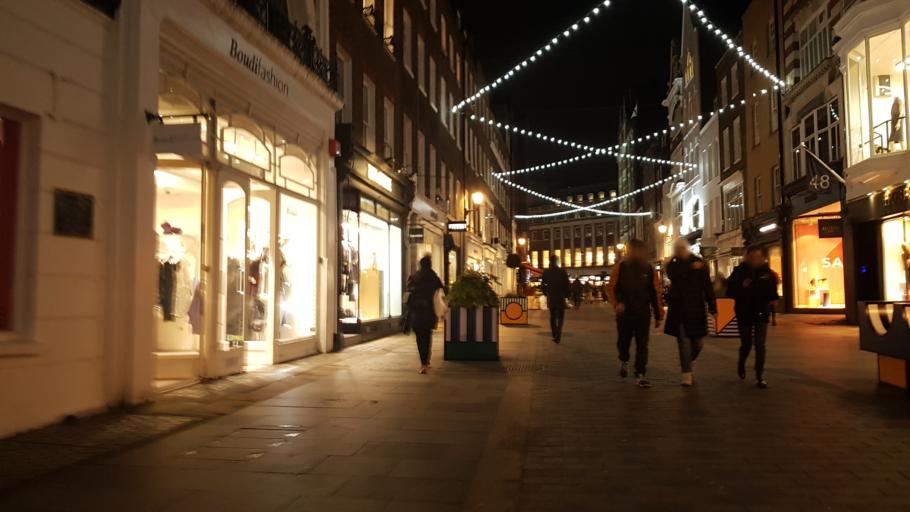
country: GB
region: England
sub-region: Greater London
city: London
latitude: 51.5137
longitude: -0.1477
